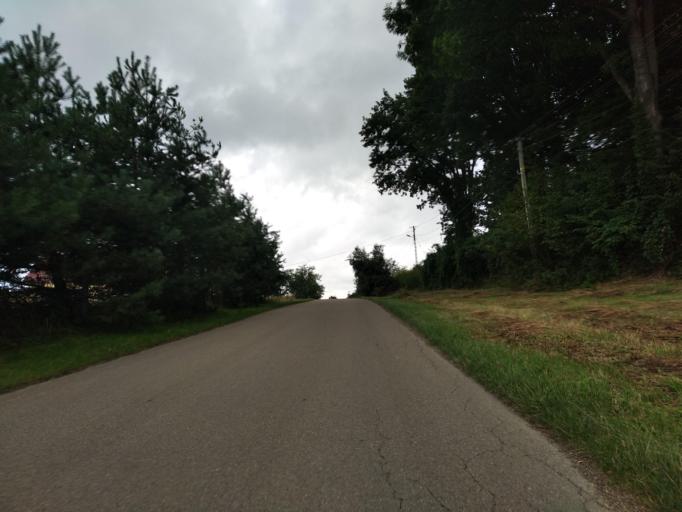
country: PL
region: Subcarpathian Voivodeship
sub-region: Powiat brzozowski
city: Dydnia
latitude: 49.6738
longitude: 22.2773
